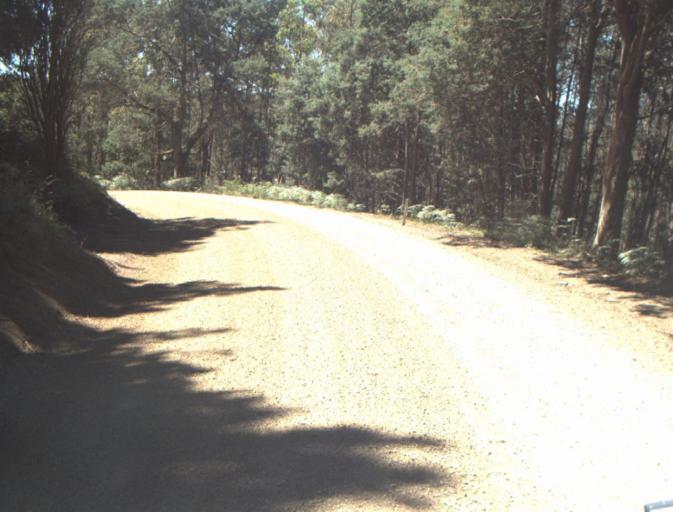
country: AU
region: Tasmania
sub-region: Dorset
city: Scottsdale
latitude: -41.3215
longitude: 147.4541
